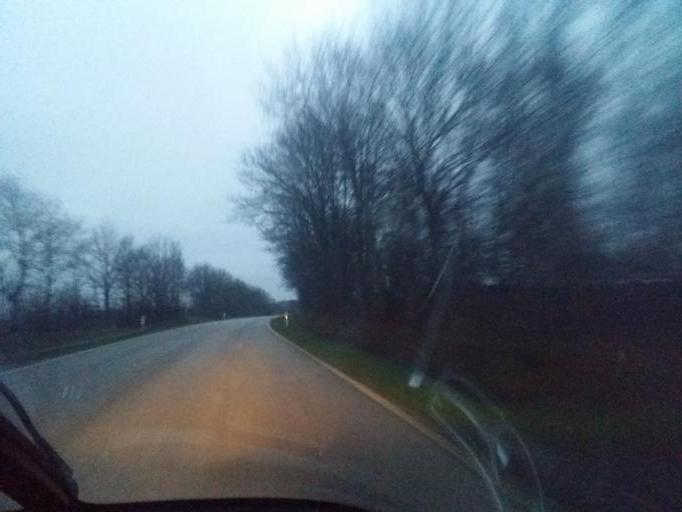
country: DE
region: Schleswig-Holstein
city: Schenefeld
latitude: 54.0646
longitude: 9.4735
